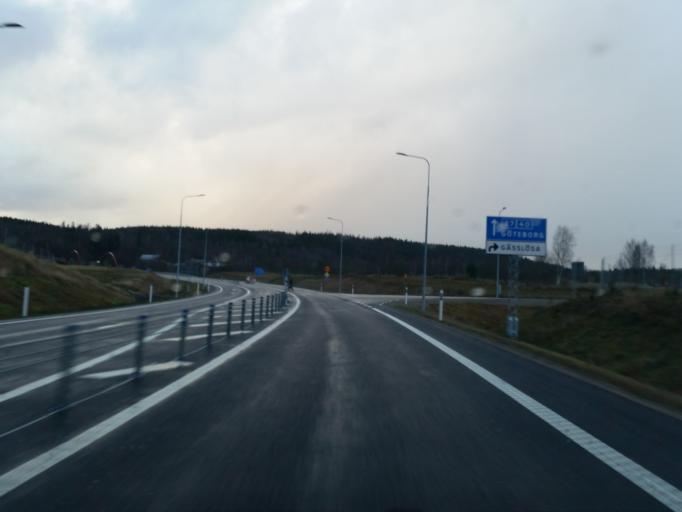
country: SE
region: Vaestra Goetaland
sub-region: Boras Kommun
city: Boras
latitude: 57.6946
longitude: 12.9184
